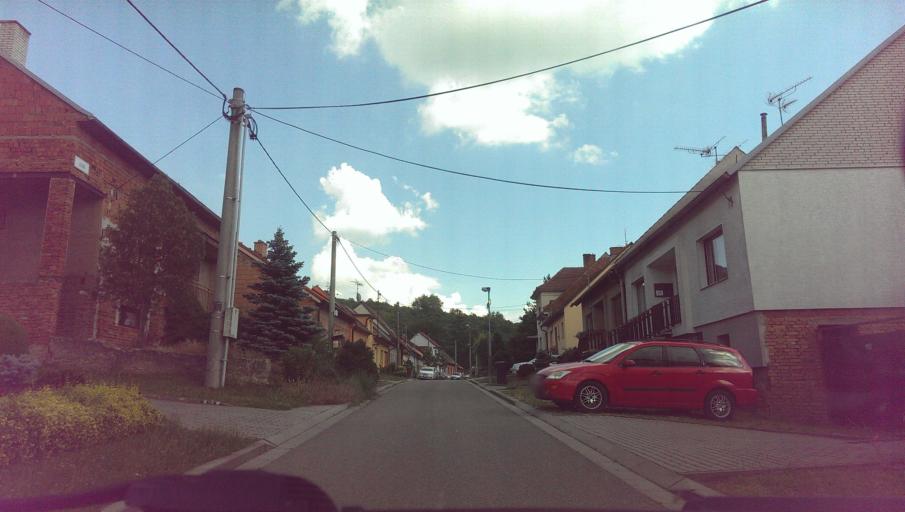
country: CZ
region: Zlin
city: Popovice
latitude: 49.0338
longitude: 17.5098
